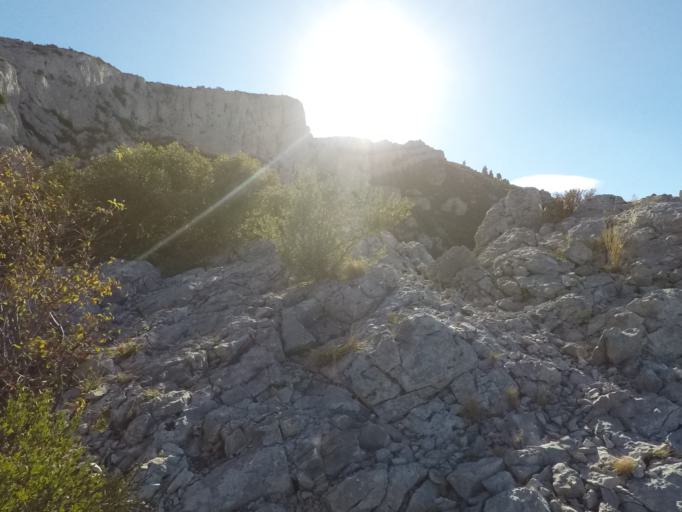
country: FR
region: Provence-Alpes-Cote d'Azur
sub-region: Departement des Bouches-du-Rhone
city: La Penne-sur-Huveaune
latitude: 43.2683
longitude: 5.4902
